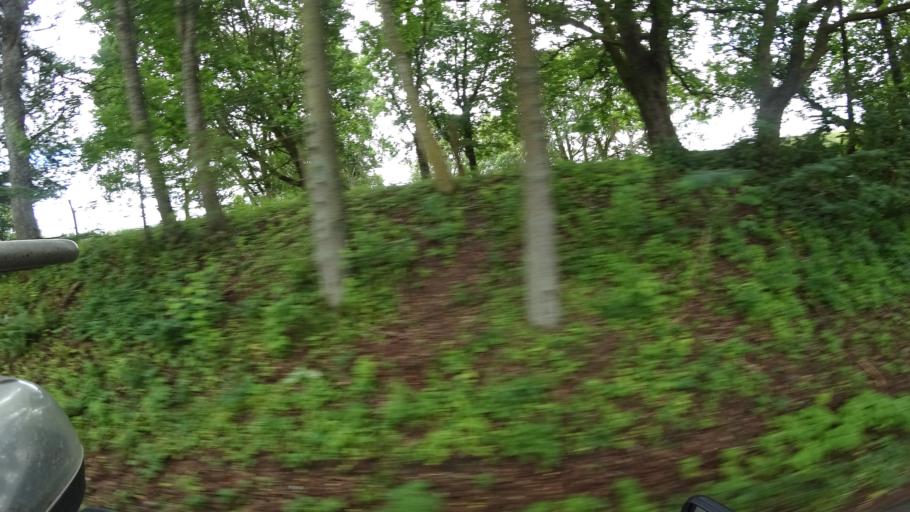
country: SE
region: Skane
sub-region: Kristianstads Kommun
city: Degeberga
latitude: 55.7156
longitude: 13.9873
